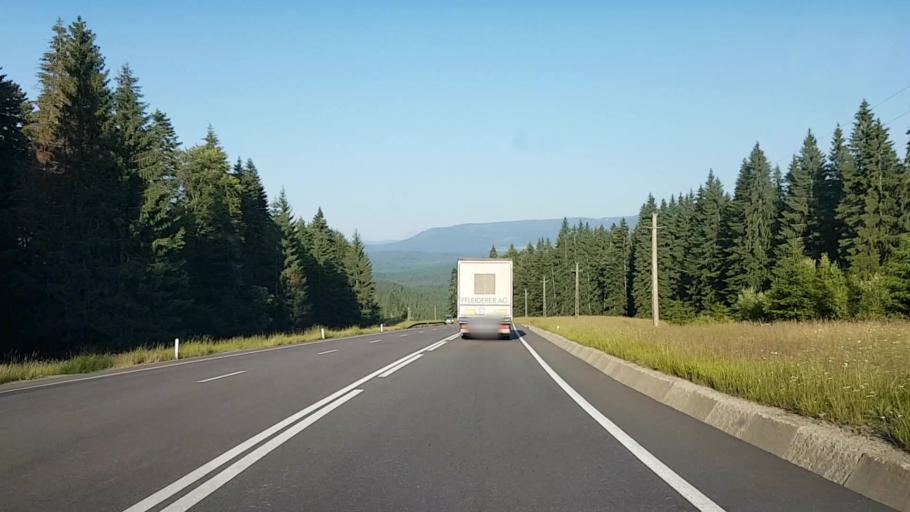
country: RO
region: Suceava
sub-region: Comuna Poiana Stampei
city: Poiana Stampei
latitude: 47.2844
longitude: 25.0458
